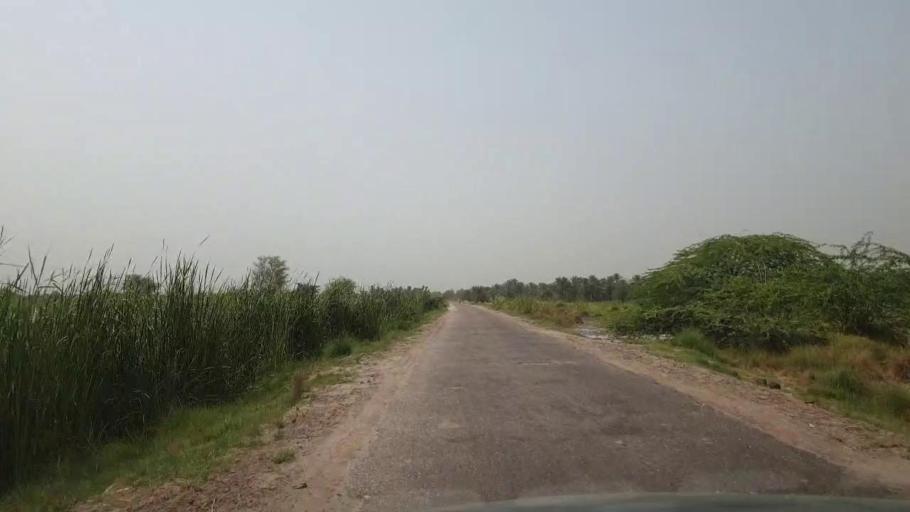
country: PK
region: Sindh
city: Gambat
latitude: 27.3850
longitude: 68.5486
